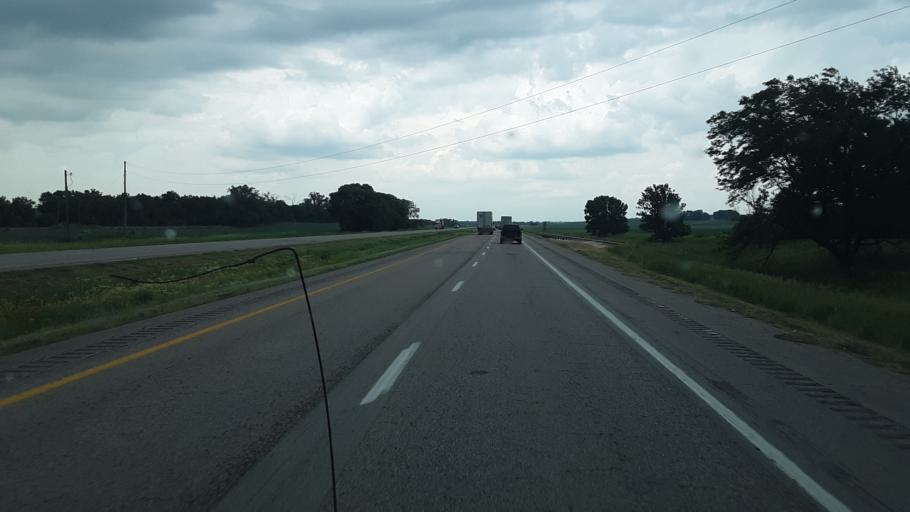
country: US
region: Iowa
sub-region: Pottawattamie County
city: Council Bluffs
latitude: 41.4103
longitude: -95.6509
